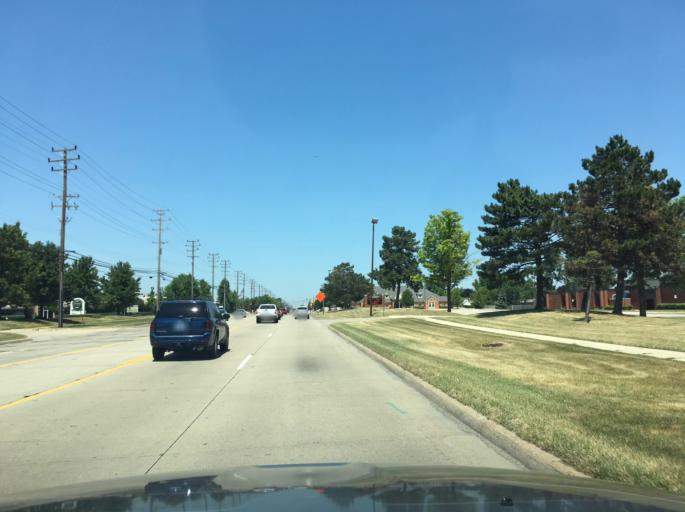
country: US
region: Michigan
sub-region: Macomb County
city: Clinton
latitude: 42.5861
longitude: -82.9519
